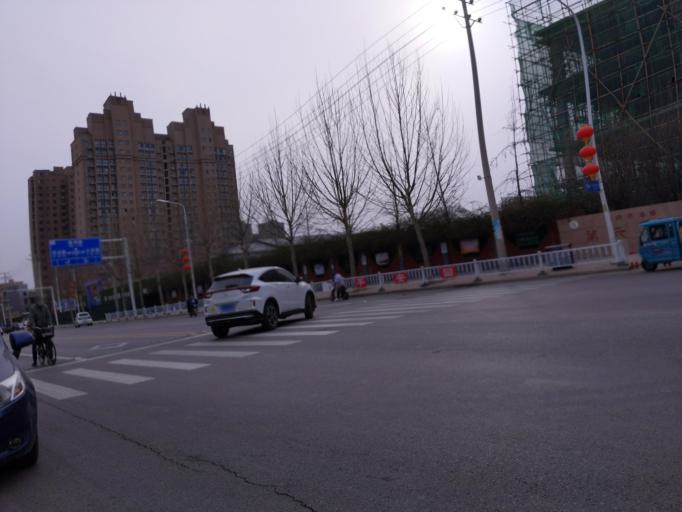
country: CN
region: Henan Sheng
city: Zhongyuanlu
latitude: 35.7621
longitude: 115.0745
